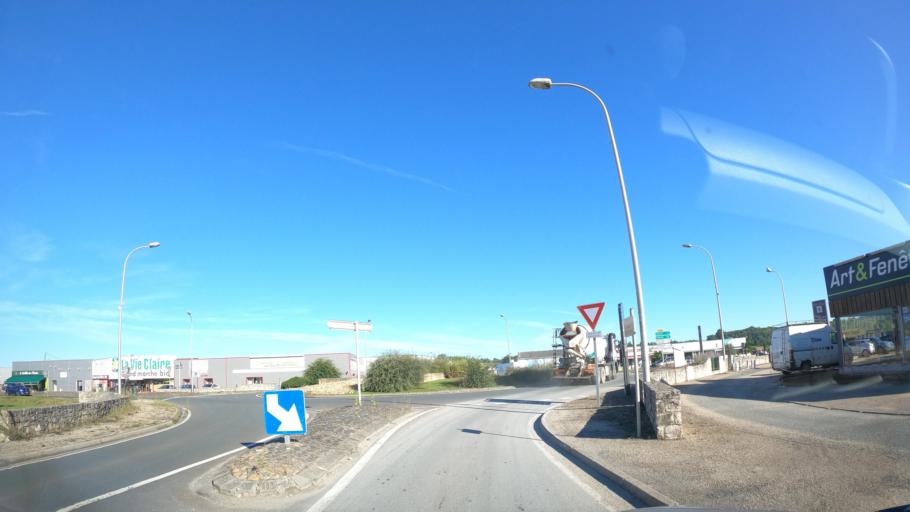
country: FR
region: Aquitaine
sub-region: Departement de la Dordogne
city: Cours-de-Pile
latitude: 44.8497
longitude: 0.5371
